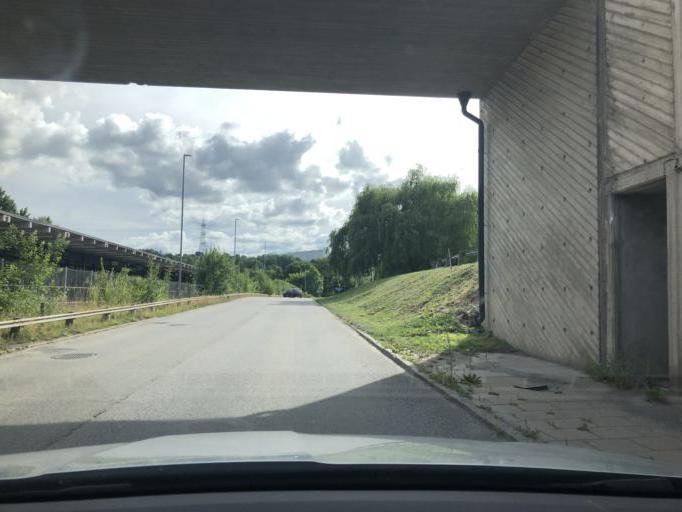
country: SE
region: Stockholm
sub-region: Botkyrka Kommun
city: Fittja
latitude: 59.2478
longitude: 17.8608
